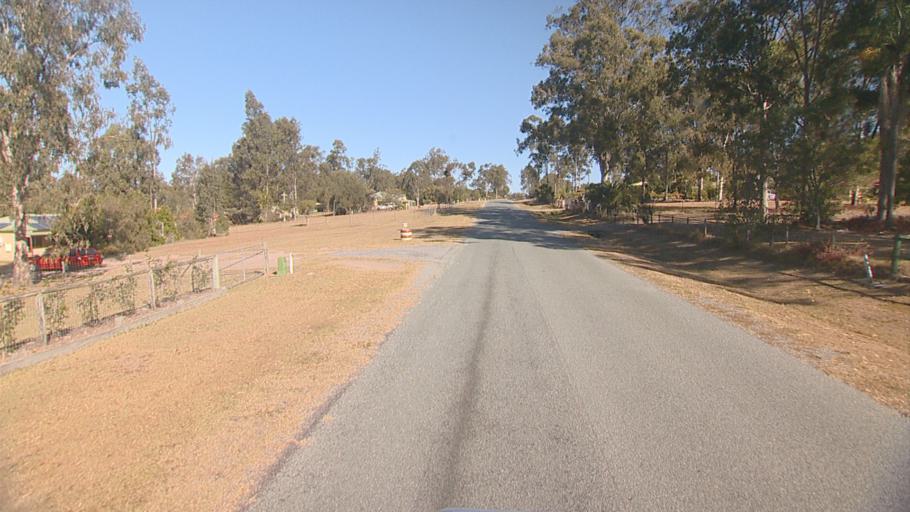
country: AU
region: Queensland
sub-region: Logan
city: Cedar Vale
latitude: -27.8615
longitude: 153.0356
